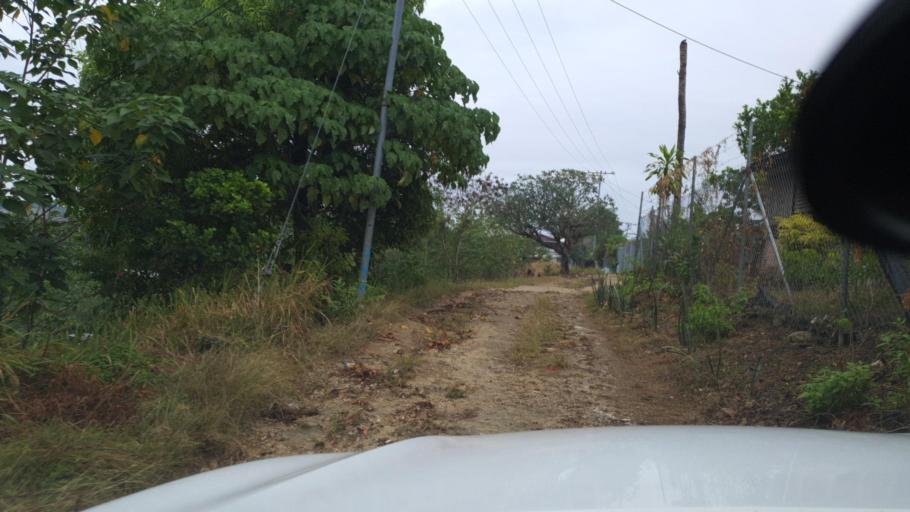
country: SB
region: Guadalcanal
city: Honiara
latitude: -9.4423
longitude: 159.9692
